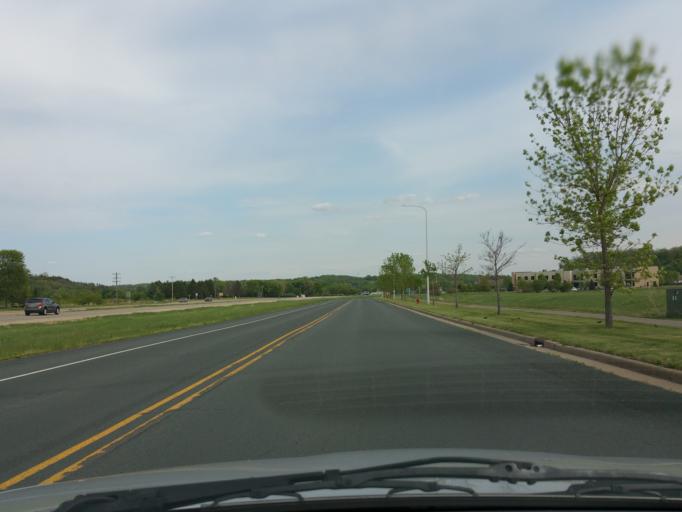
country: US
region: Wisconsin
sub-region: Pierce County
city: River Falls
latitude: 44.8905
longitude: -92.6348
